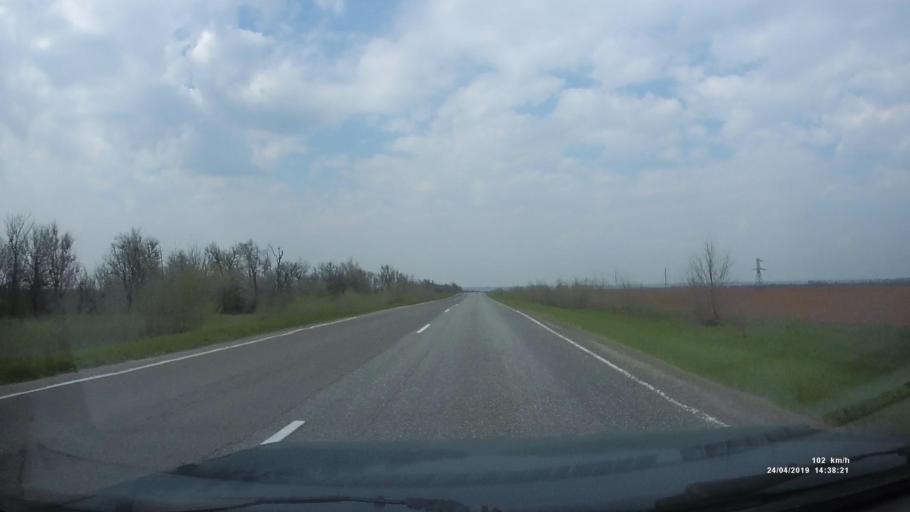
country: RU
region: Rostov
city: Remontnoye
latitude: 46.3998
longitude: 43.8861
